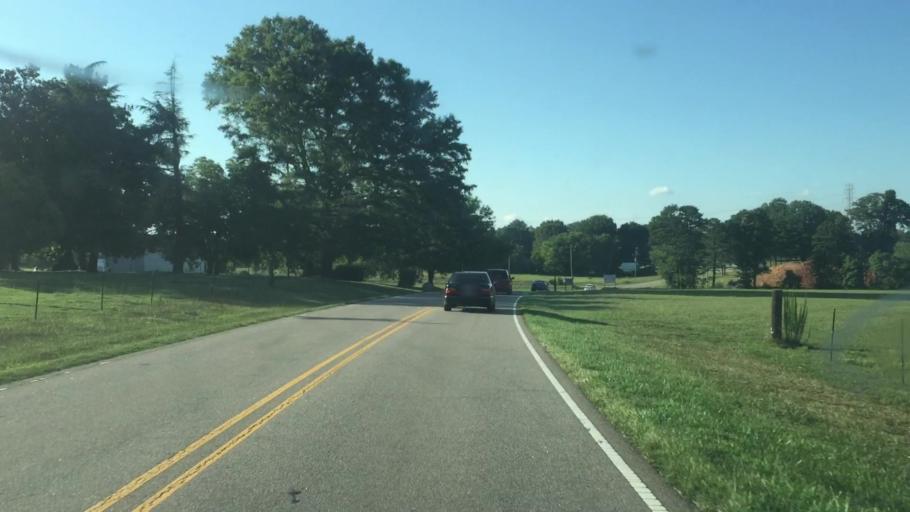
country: US
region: North Carolina
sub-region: Gaston County
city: Davidson
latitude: 35.4968
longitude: -80.7697
